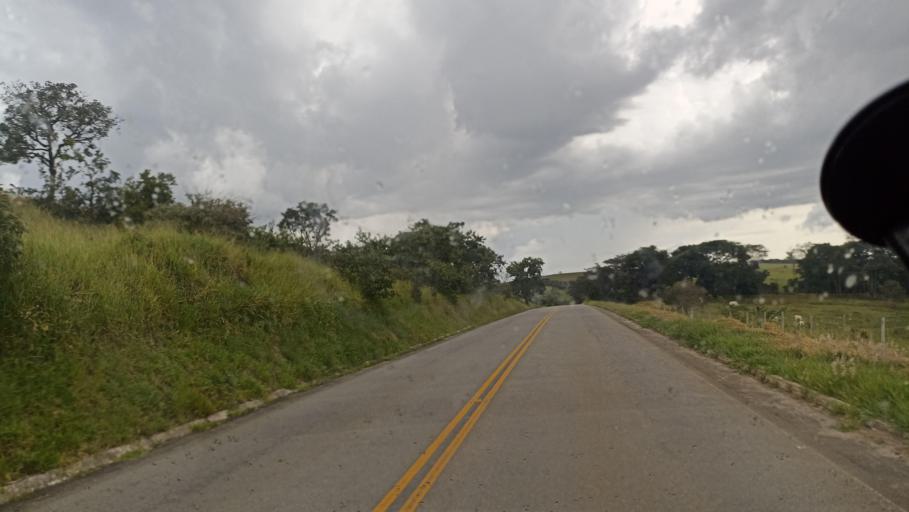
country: BR
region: Minas Gerais
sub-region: Cruzilia
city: Cruzilia
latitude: -21.9161
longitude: -44.8235
